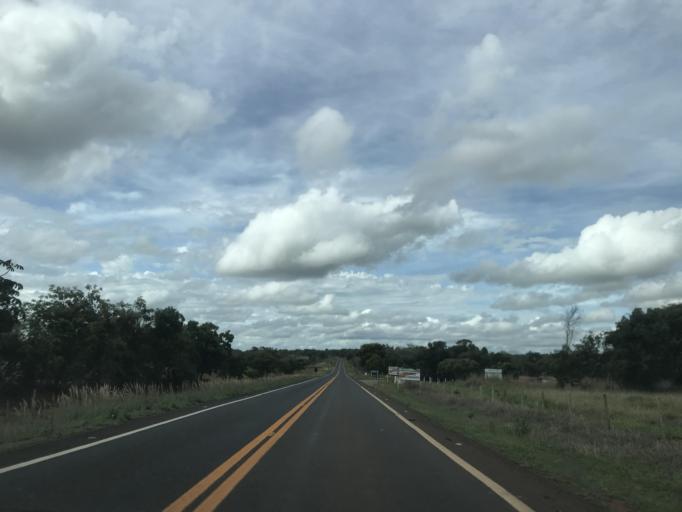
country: BR
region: Goias
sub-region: Piracanjuba
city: Piracanjuba
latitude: -17.4034
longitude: -48.8060
